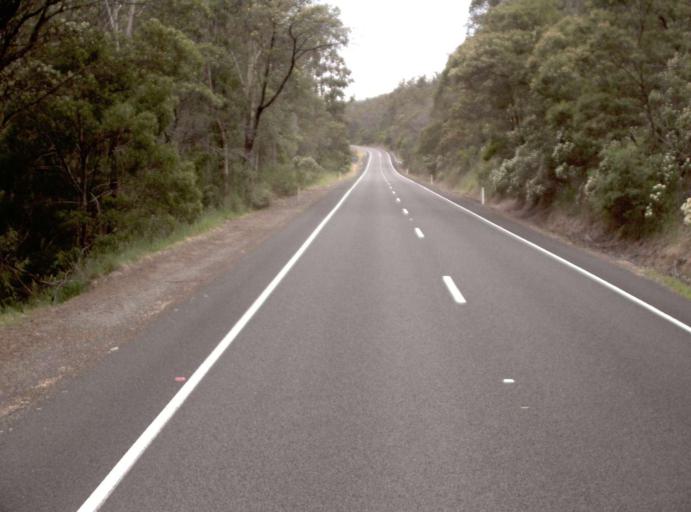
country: AU
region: New South Wales
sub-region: Bombala
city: Bombala
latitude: -37.2533
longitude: 149.2459
